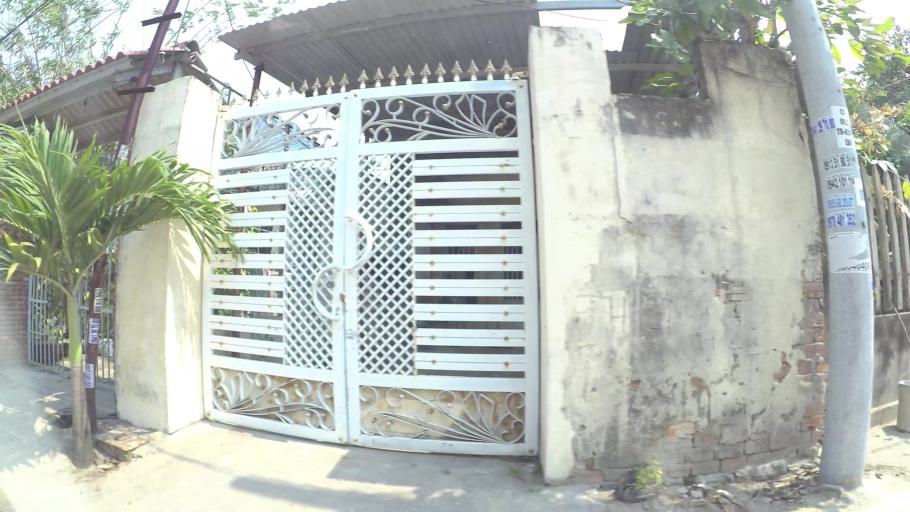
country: VN
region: Da Nang
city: Ngu Hanh Son
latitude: 16.0076
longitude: 108.2550
